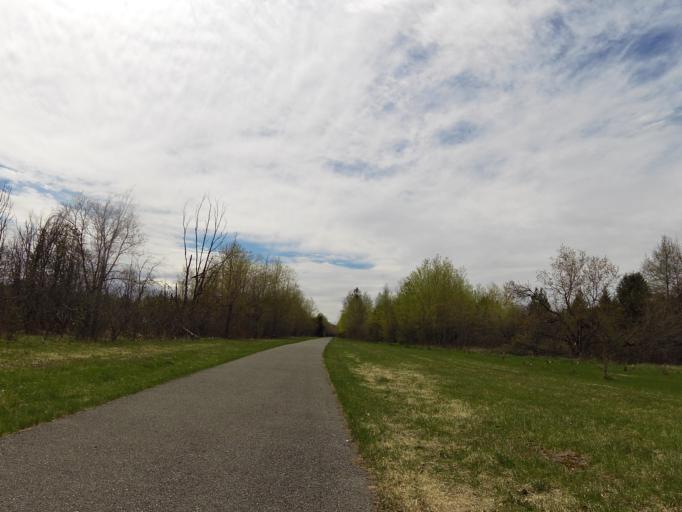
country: CA
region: Ontario
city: Hawkesbury
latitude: 45.5346
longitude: -74.6458
